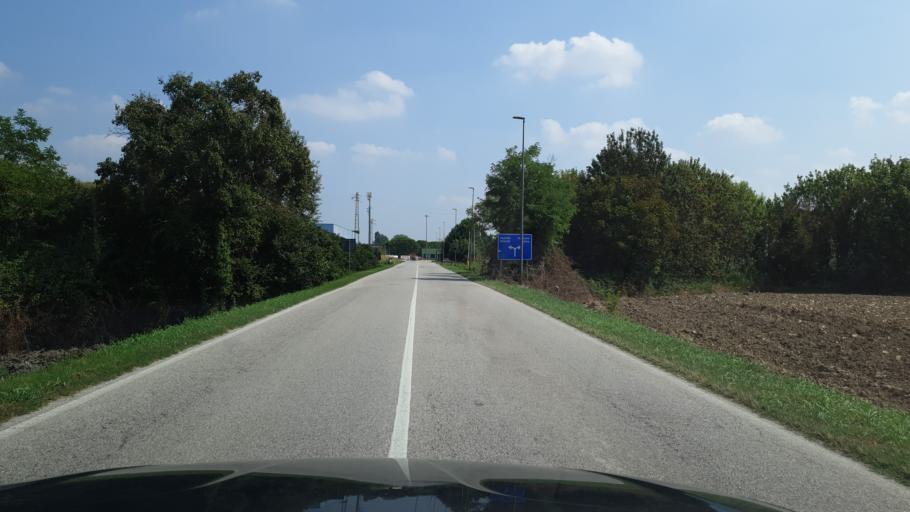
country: IT
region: Veneto
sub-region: Provincia di Rovigo
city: Bosaro
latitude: 45.0078
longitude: 11.7618
